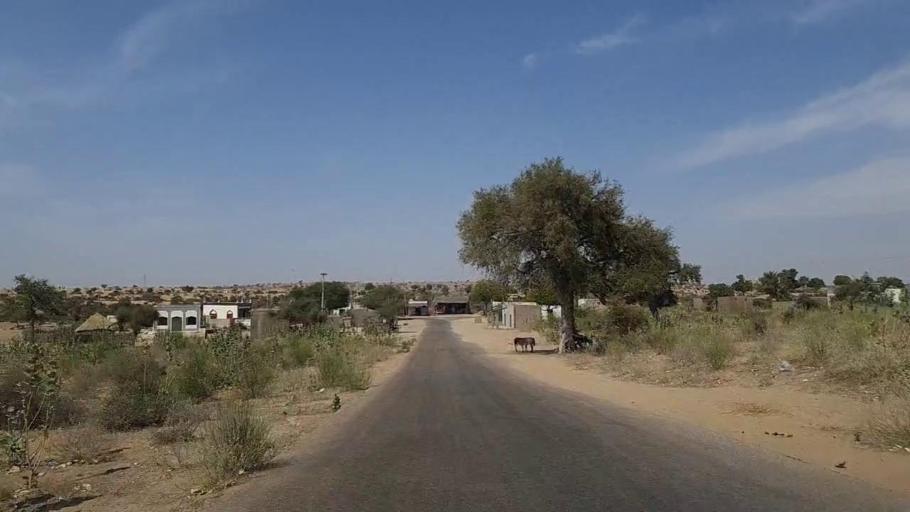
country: PK
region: Sindh
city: Umarkot
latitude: 25.1614
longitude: 70.0065
